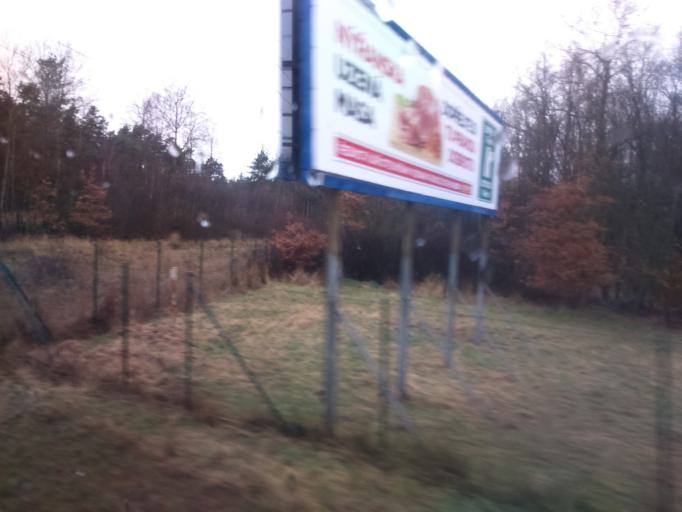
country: CZ
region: Plzensky
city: Vejprnice
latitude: 49.7264
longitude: 13.3083
